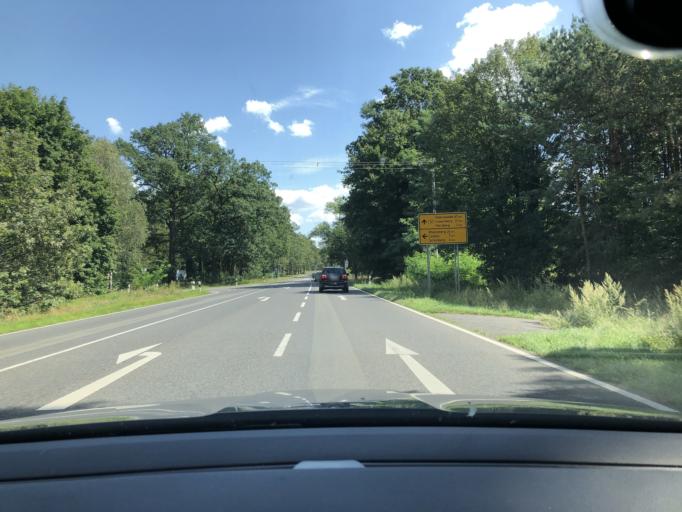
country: DE
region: Brandenburg
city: Lindow
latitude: 52.9257
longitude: 12.9198
